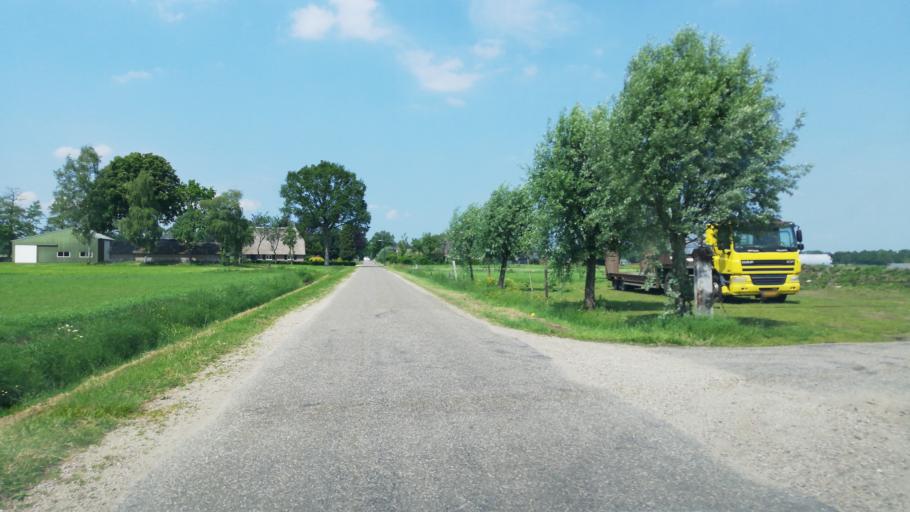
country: NL
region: Gelderland
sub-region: Gemeente Epe
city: Vaassen
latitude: 52.2599
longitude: 5.9898
